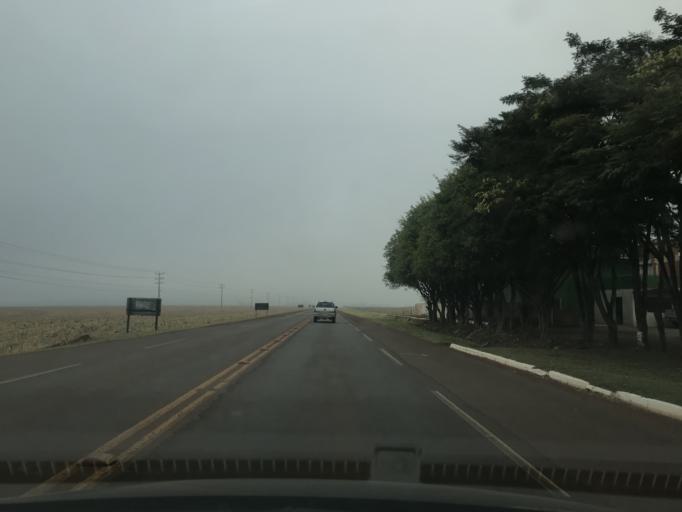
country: BR
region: Parana
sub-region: Toledo
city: Toledo
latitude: -24.6864
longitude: -53.6958
